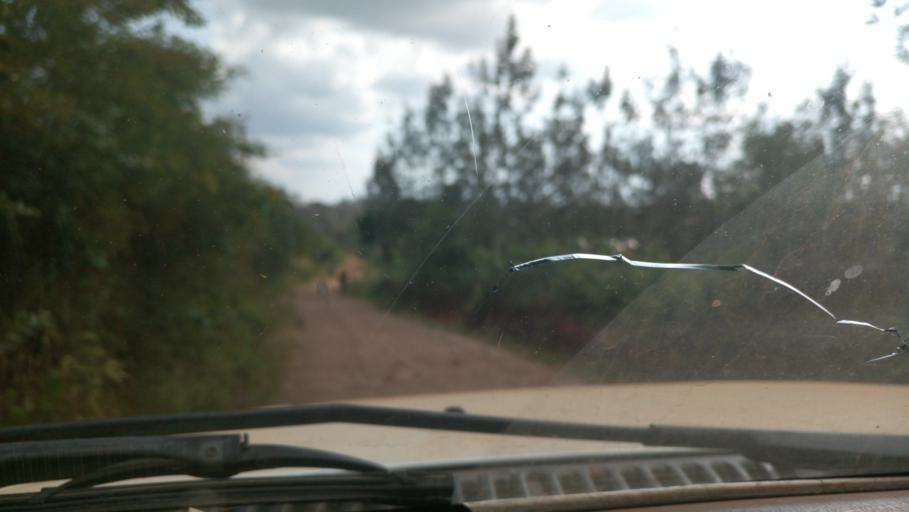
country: KE
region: Murang'a District
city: Maragua
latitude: -0.9055
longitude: 37.1105
